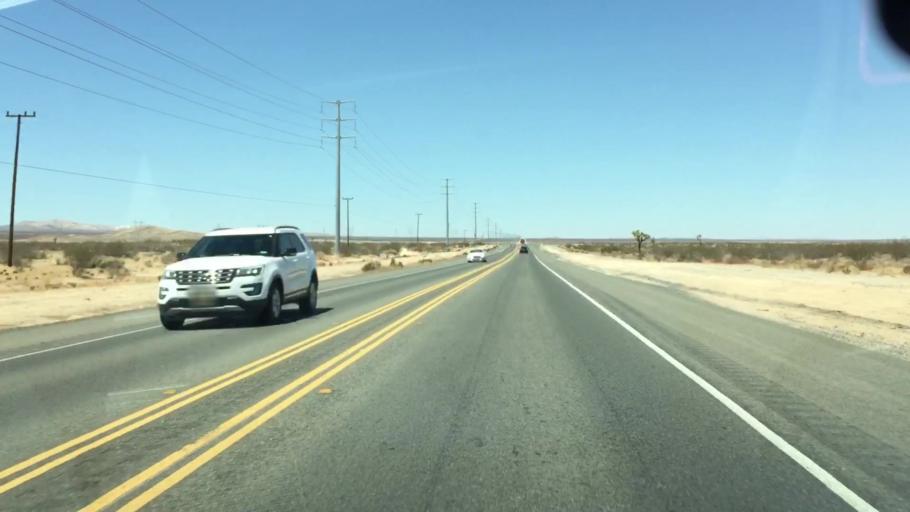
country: US
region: California
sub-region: San Bernardino County
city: Adelanto
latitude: 34.6419
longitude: -117.4336
